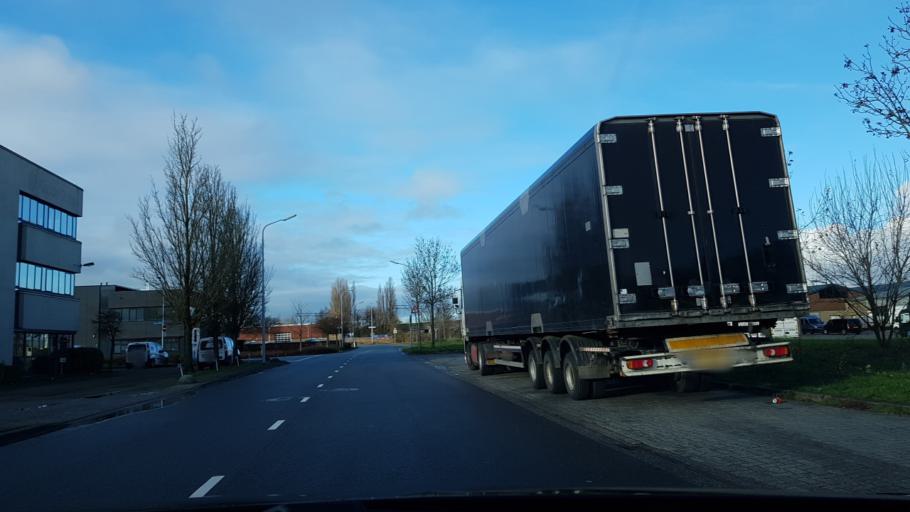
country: NL
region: North Holland
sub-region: Gemeente Haarlemmermeer
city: Hoofddorp
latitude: 52.2939
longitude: 4.7191
